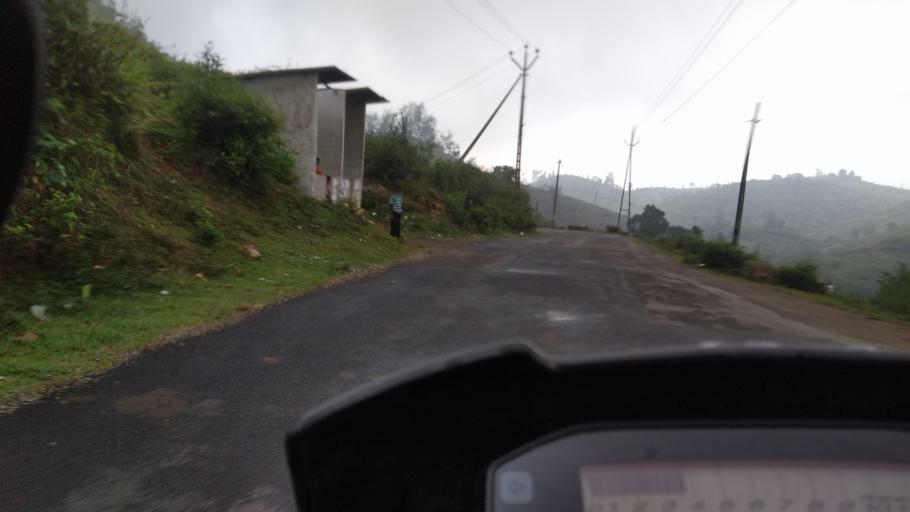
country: IN
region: Kerala
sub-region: Kottayam
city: Erattupetta
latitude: 9.6314
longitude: 76.9425
